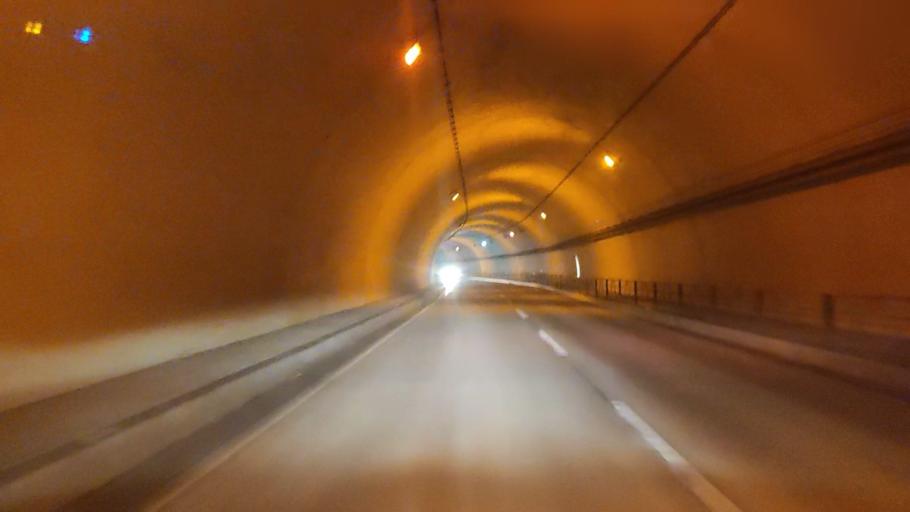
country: JP
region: Miyazaki
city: Nobeoka
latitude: 32.6927
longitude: 131.8110
